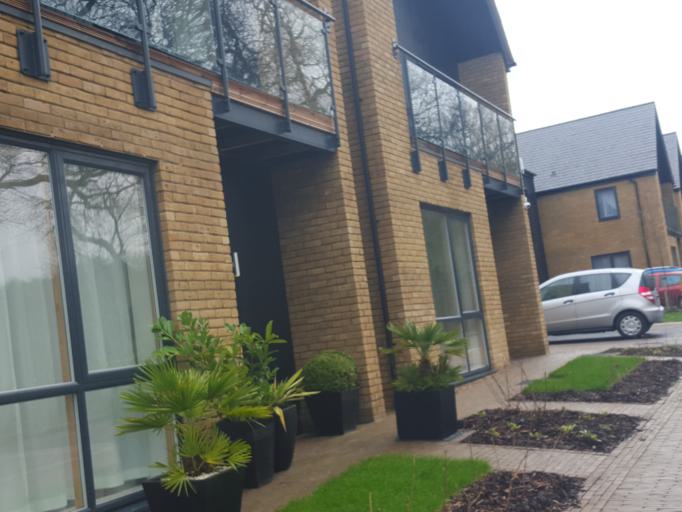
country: GB
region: England
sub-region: Essex
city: Harlow
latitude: 51.7716
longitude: 0.1398
